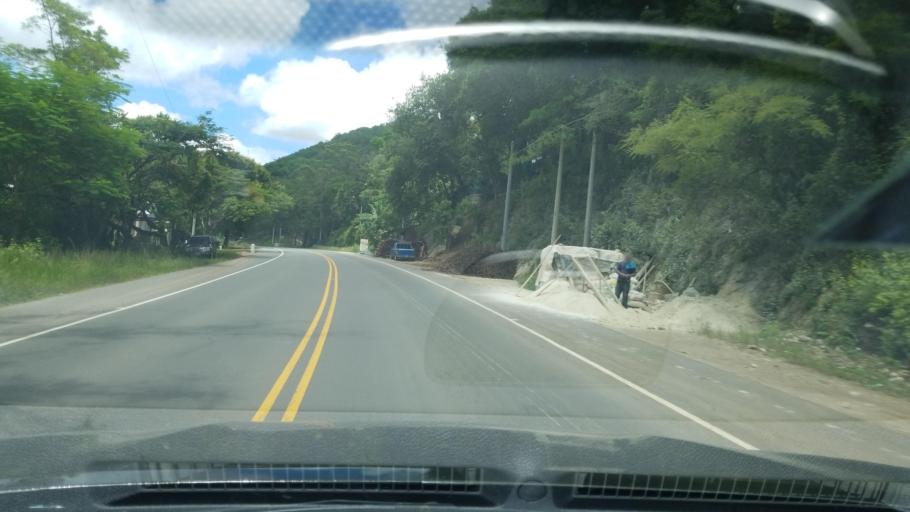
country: HN
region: Francisco Morazan
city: Talanga
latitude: 14.3781
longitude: -87.1372
